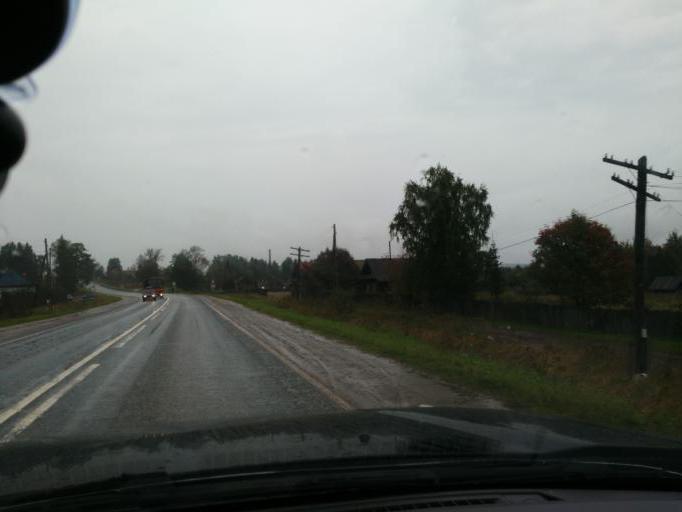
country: RU
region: Perm
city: Yugo-Kamskiy
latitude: 57.5519
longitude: 55.6855
